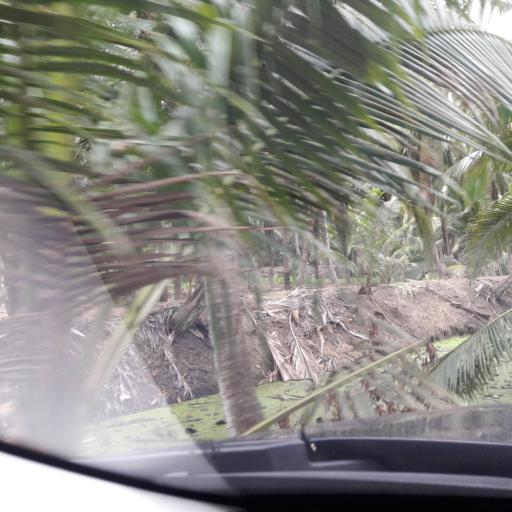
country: TH
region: Ratchaburi
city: Damnoen Saduak
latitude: 13.5824
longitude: 99.9435
